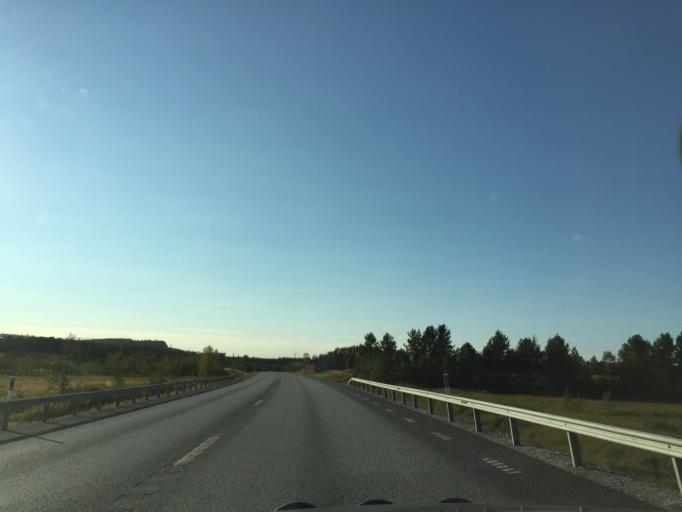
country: SE
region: Norrbotten
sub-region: Gallivare Kommun
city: Malmberget
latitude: 67.6444
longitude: 21.0479
